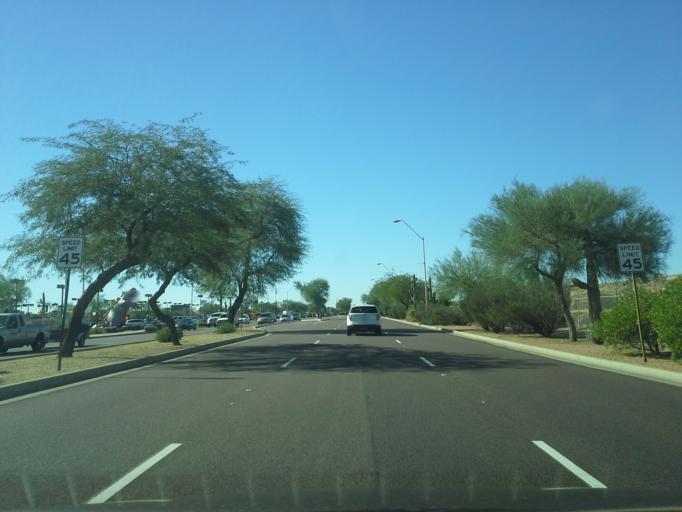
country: US
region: Arizona
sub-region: Maricopa County
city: Paradise Valley
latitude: 33.6350
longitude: -111.9099
